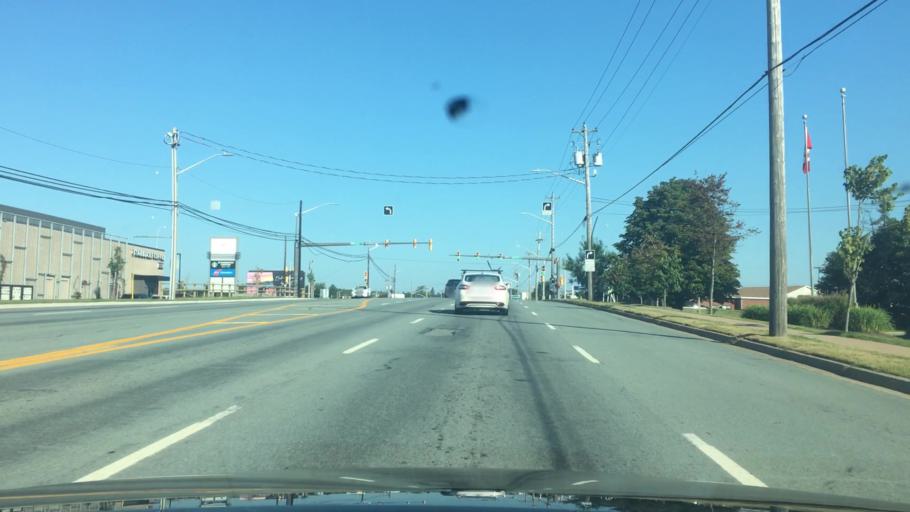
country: CA
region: Nova Scotia
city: Dartmouth
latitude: 44.6998
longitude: -63.6063
